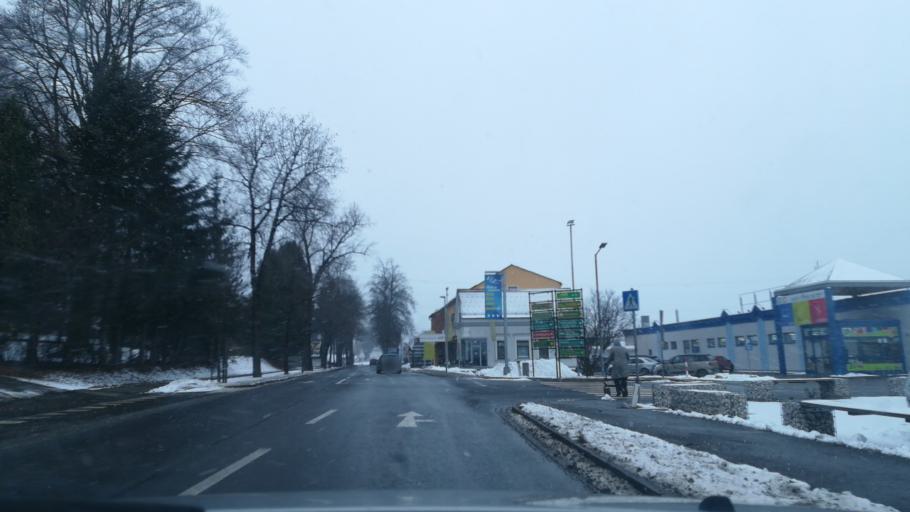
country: AT
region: Styria
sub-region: Politischer Bezirk Murtal
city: Oberweg
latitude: 47.1714
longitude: 14.6353
